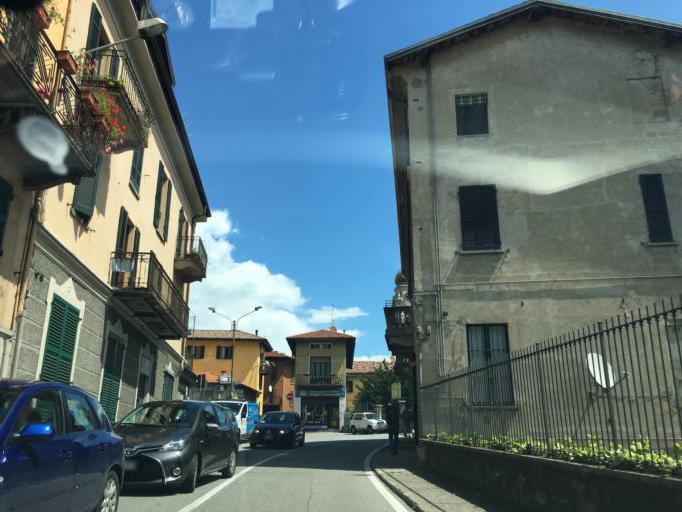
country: IT
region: Lombardy
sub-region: Provincia di Como
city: Menaggio
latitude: 46.0194
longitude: 9.2369
